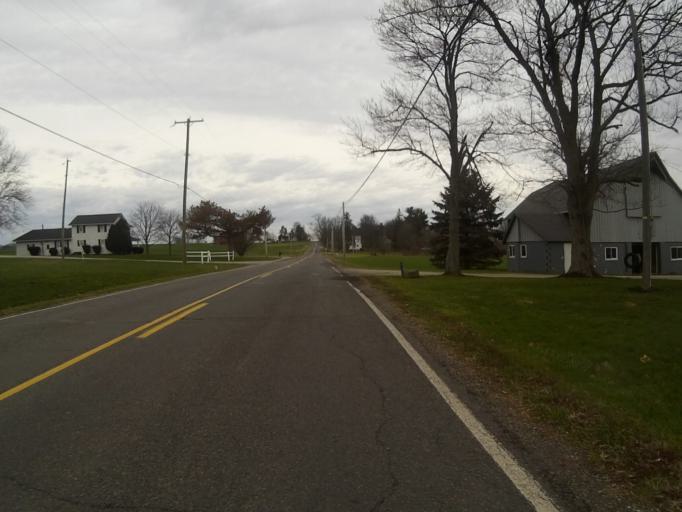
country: US
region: Ohio
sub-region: Stark County
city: Hartville
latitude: 41.0063
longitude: -81.3294
